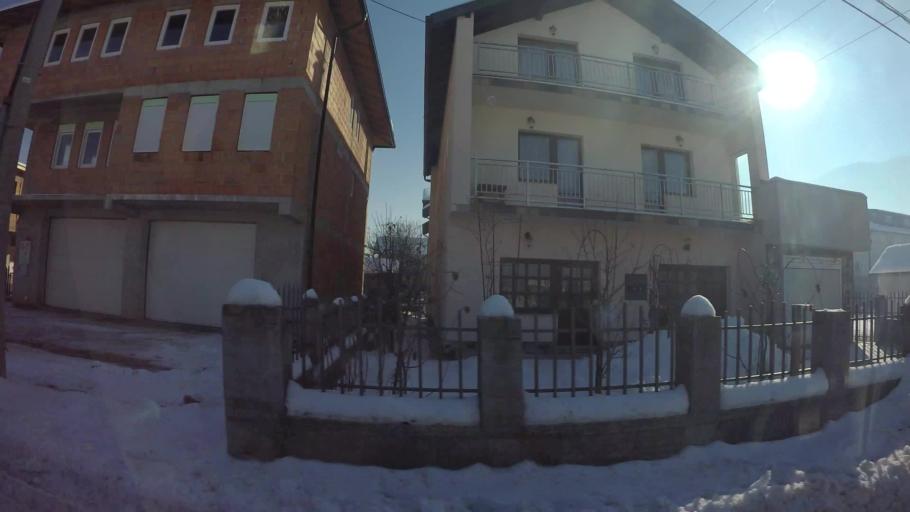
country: BA
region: Federation of Bosnia and Herzegovina
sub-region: Kanton Sarajevo
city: Sarajevo
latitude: 43.8091
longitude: 18.3001
